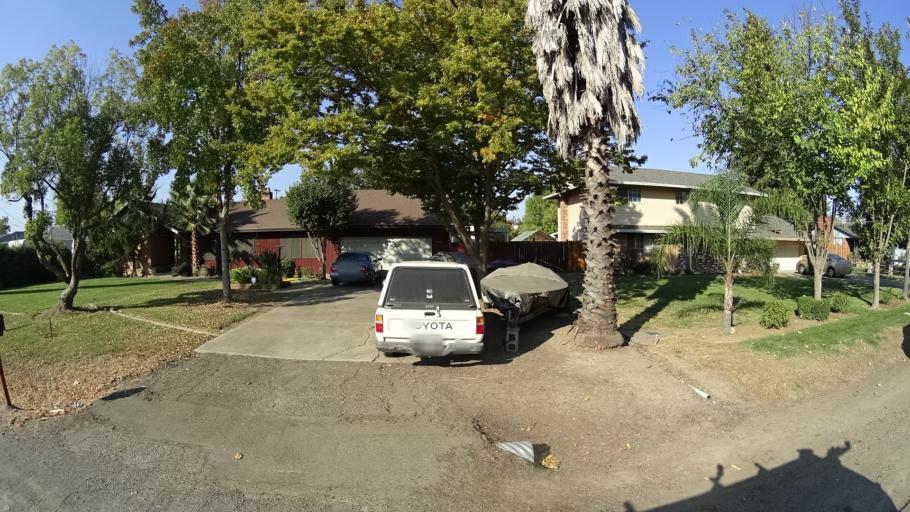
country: US
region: California
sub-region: Sacramento County
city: Parkway
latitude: 38.4868
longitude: -121.4968
